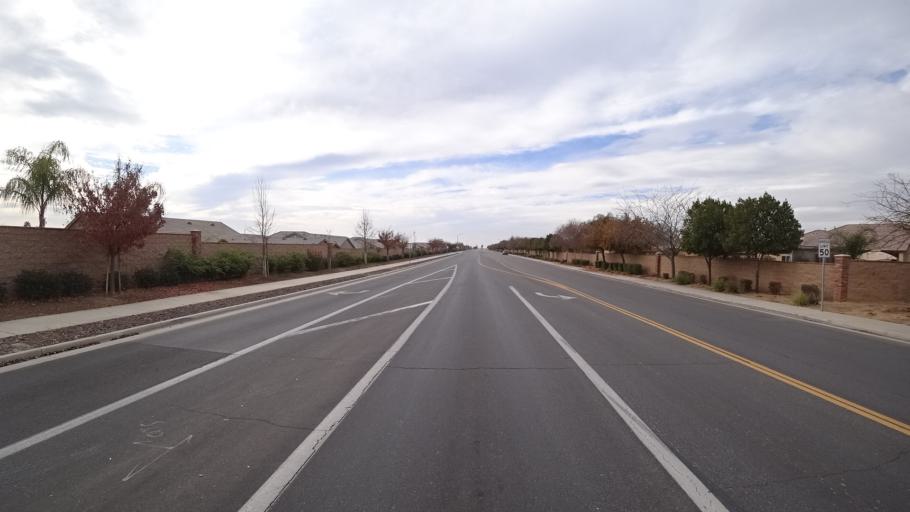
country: US
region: California
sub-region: Kern County
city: Rosedale
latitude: 35.4124
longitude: -119.1458
